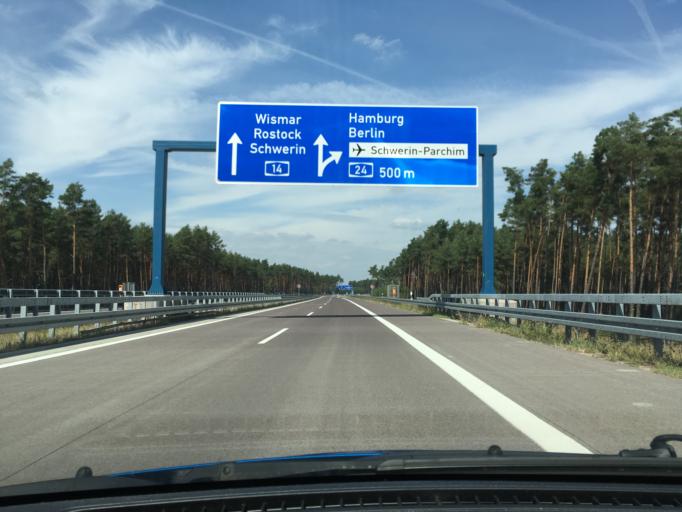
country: DE
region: Mecklenburg-Vorpommern
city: Gross Laasch
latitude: 53.4117
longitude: 11.5272
